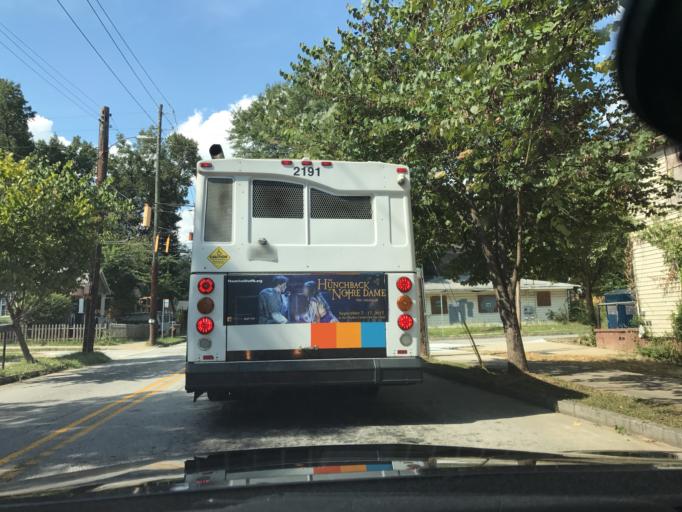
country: US
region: Georgia
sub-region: Fulton County
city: Atlanta
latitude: 33.7253
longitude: -84.4016
